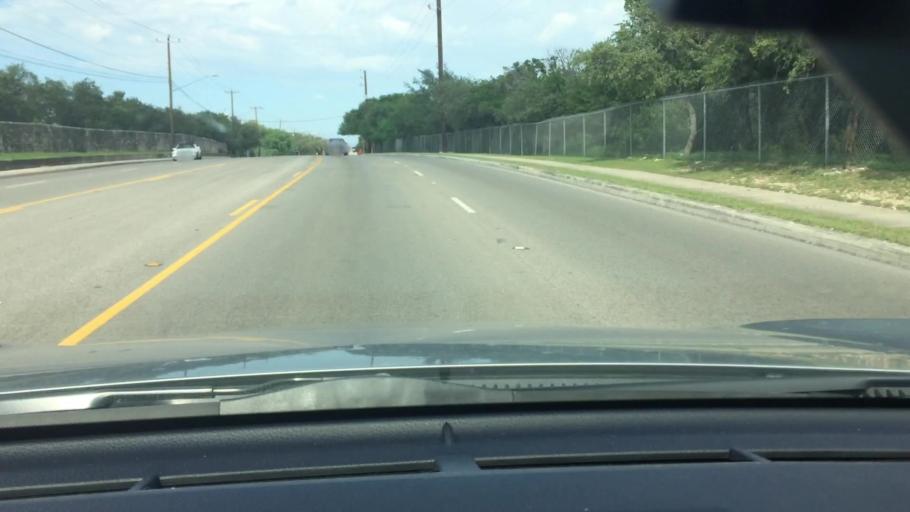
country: US
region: Texas
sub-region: Bexar County
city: Shavano Park
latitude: 29.5578
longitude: -98.5647
